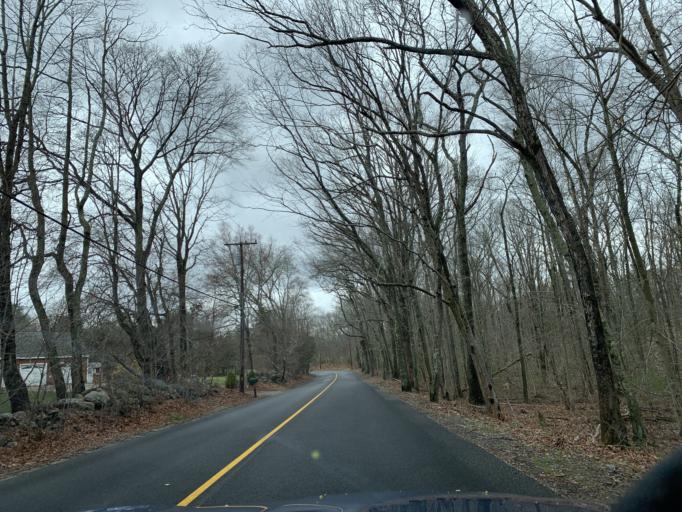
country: US
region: Massachusetts
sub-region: Bristol County
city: Rehoboth
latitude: 41.8906
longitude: -71.2104
